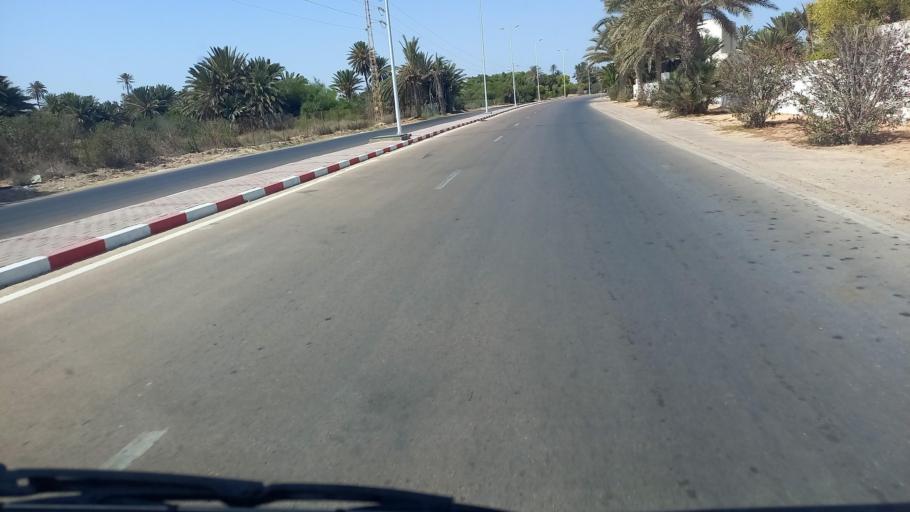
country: TN
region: Madanin
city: Midoun
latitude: 33.8256
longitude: 11.0247
